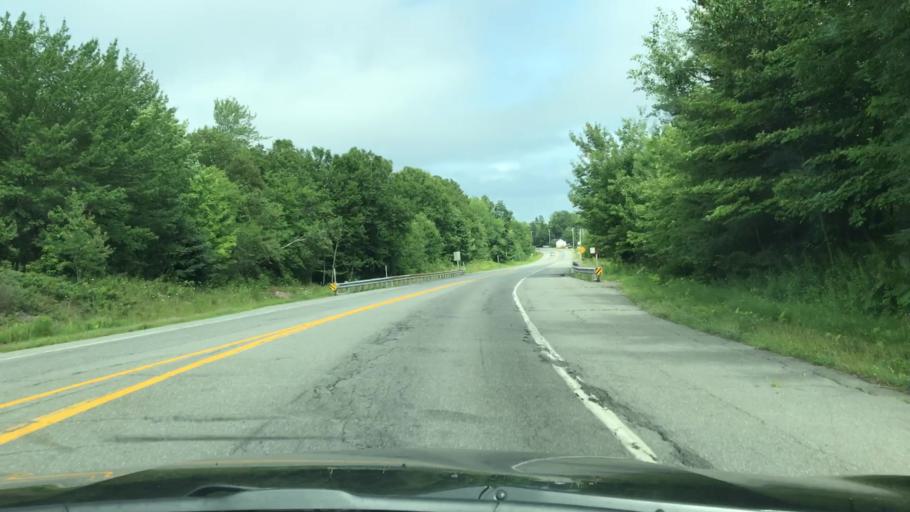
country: US
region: Maine
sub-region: Waldo County
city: Stockton Springs
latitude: 44.4932
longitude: -68.8526
